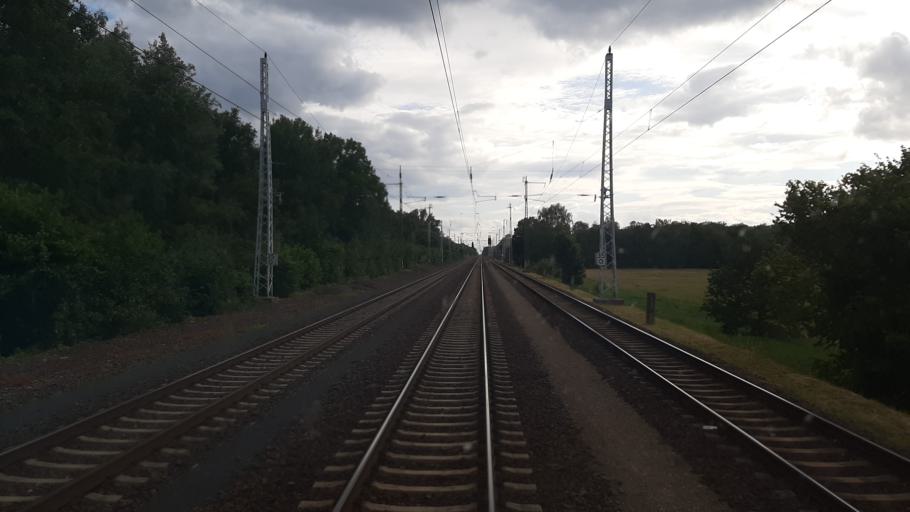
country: DE
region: Brandenburg
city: Brieselang
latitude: 52.5869
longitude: 13.0356
